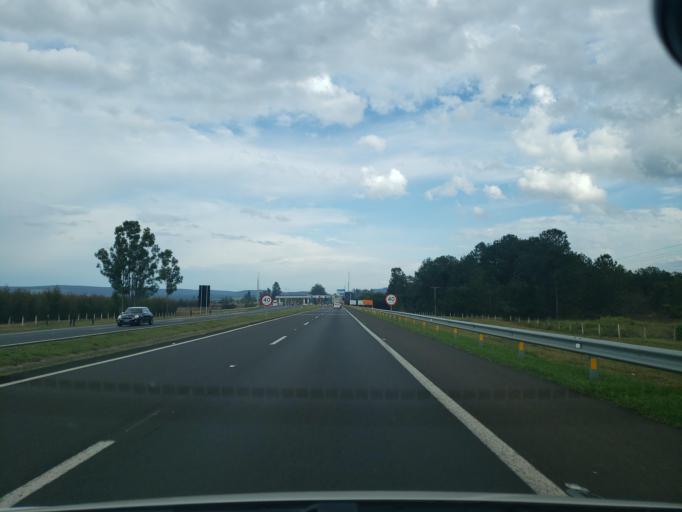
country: BR
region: Sao Paulo
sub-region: Itirapina
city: Itirapina
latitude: -22.2630
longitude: -47.8981
